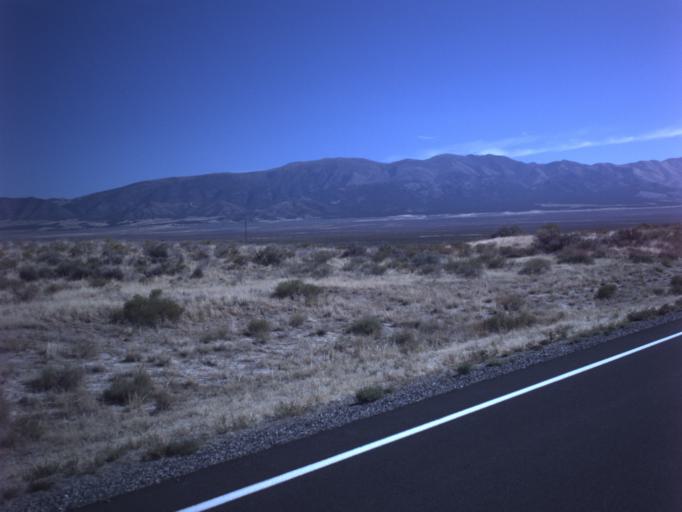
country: US
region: Utah
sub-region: Tooele County
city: Grantsville
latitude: 40.2494
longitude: -112.7293
